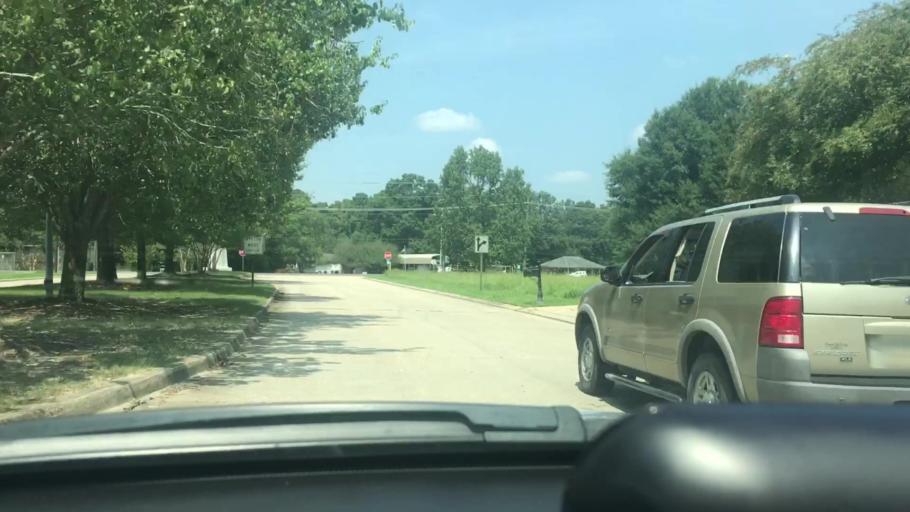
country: US
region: Louisiana
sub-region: Livingston Parish
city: Denham Springs
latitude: 30.4698
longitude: -90.9646
